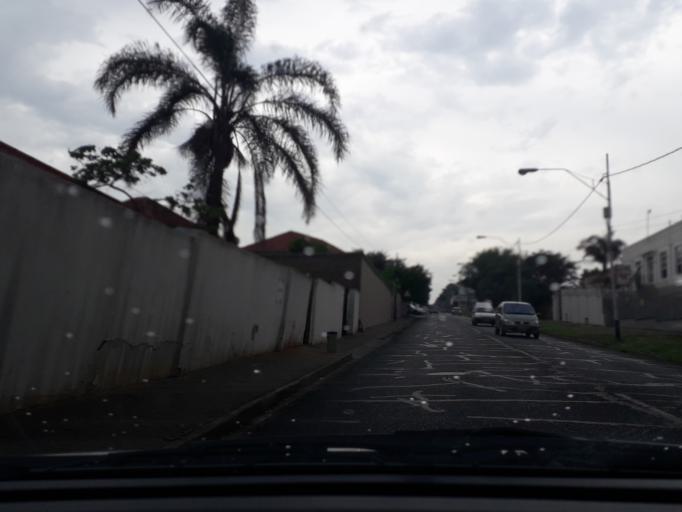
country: ZA
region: Gauteng
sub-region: City of Johannesburg Metropolitan Municipality
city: Johannesburg
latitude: -26.1488
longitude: 28.0985
